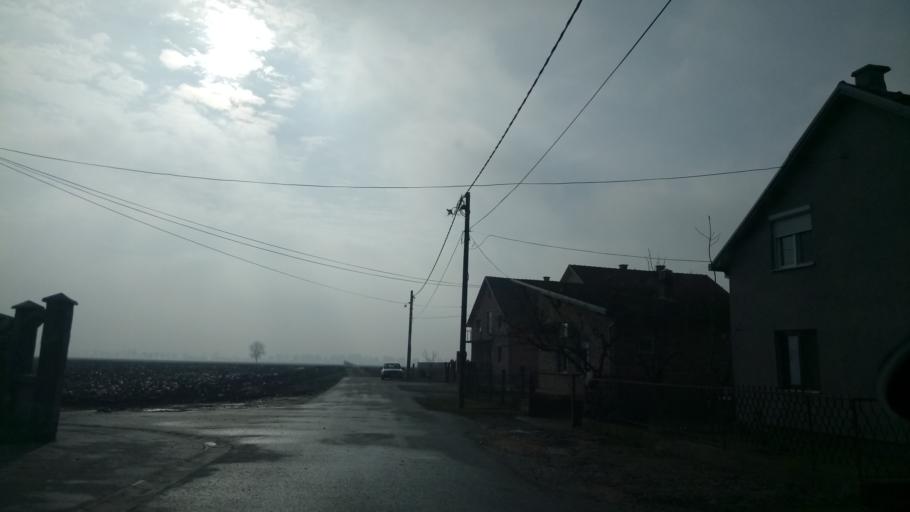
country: RS
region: Autonomna Pokrajina Vojvodina
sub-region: Sremski Okrug
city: Stara Pazova
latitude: 44.9834
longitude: 20.1829
